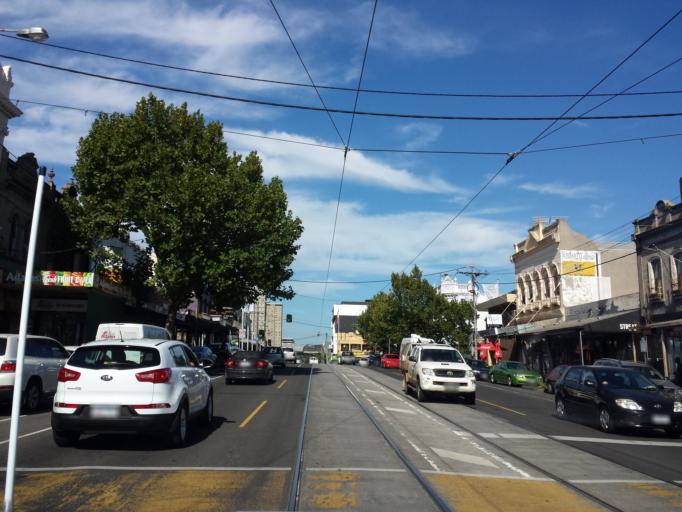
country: AU
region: Victoria
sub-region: Moonee Valley
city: Flemington
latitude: -37.7882
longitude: 144.9304
